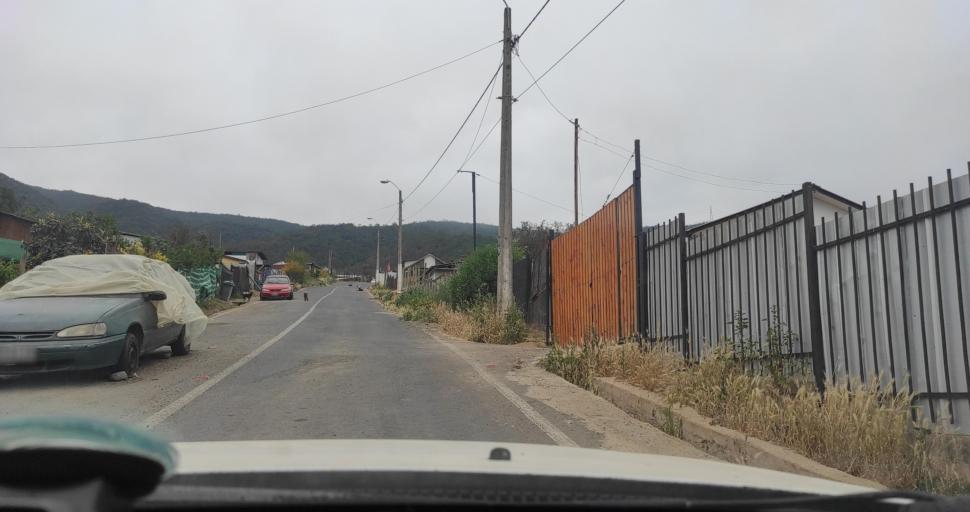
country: CL
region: Valparaiso
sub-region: Provincia de Marga Marga
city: Limache
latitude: -32.9845
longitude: -71.2266
